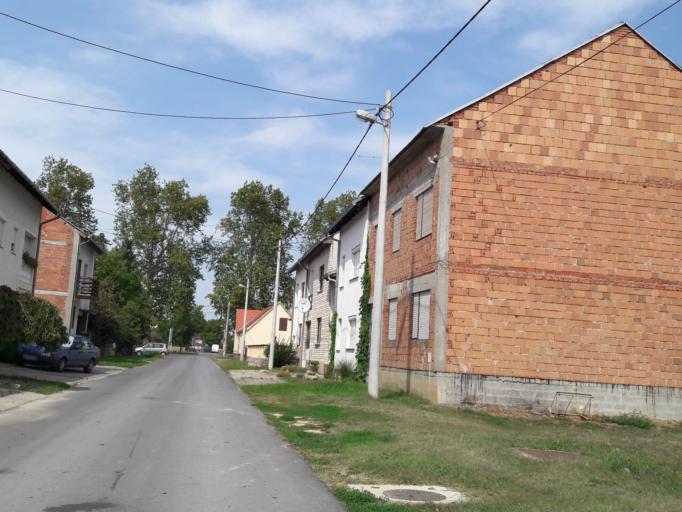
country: HR
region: Osjecko-Baranjska
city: Visnjevac
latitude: 45.5290
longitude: 18.6160
